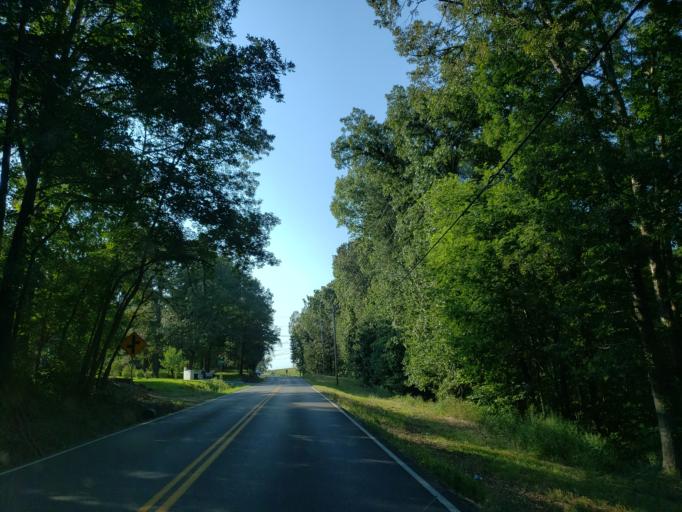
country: US
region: Tennessee
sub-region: Bradley County
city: Wildwood Lake
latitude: 35.0934
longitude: -84.7999
